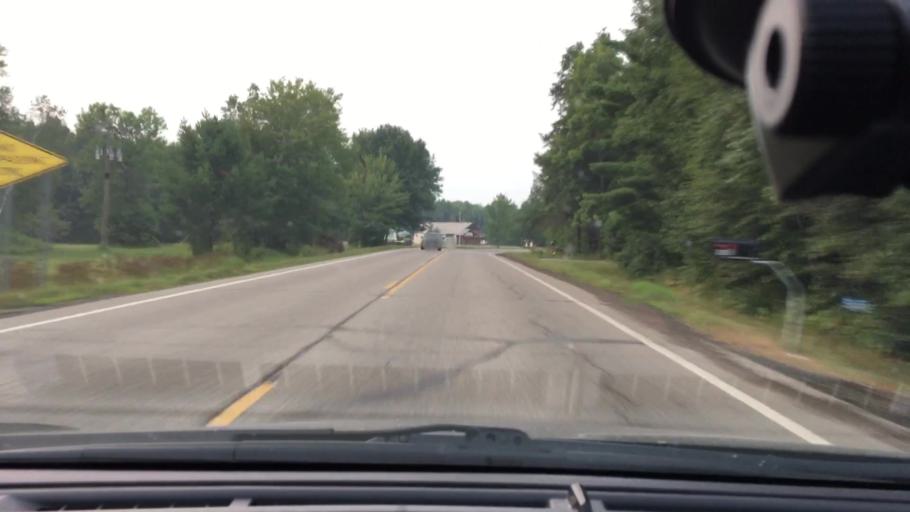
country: US
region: Minnesota
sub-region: Crow Wing County
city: Cross Lake
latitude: 46.8235
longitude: -93.9483
